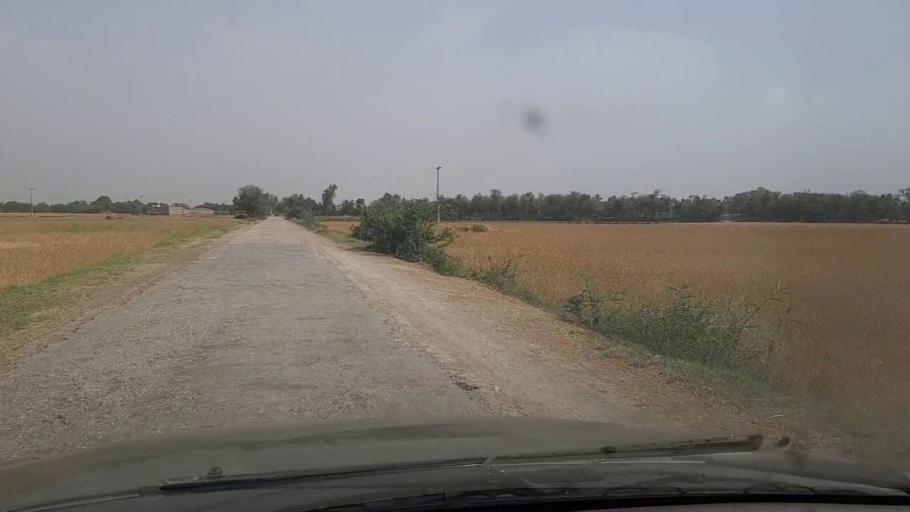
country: PK
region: Sindh
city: Lakhi
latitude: 27.8451
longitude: 68.7579
